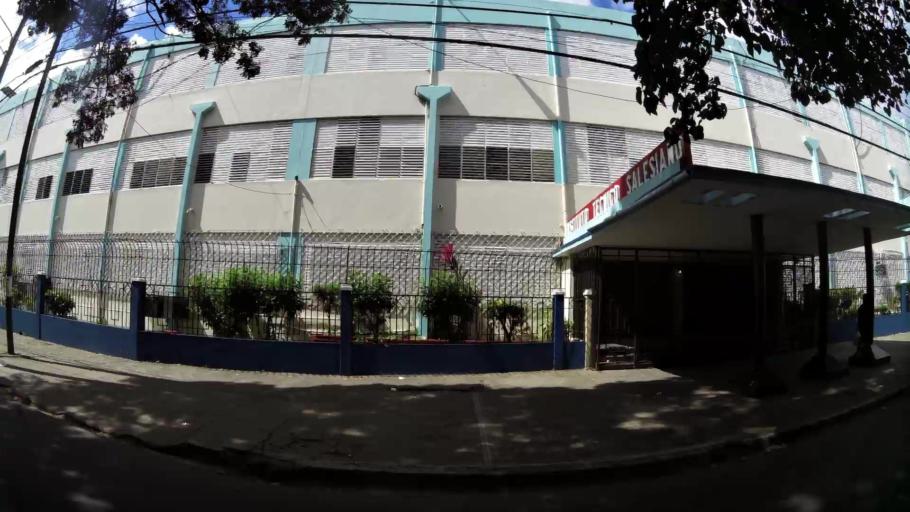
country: DO
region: Nacional
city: Ensanche Luperon
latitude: 18.4931
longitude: -69.8882
